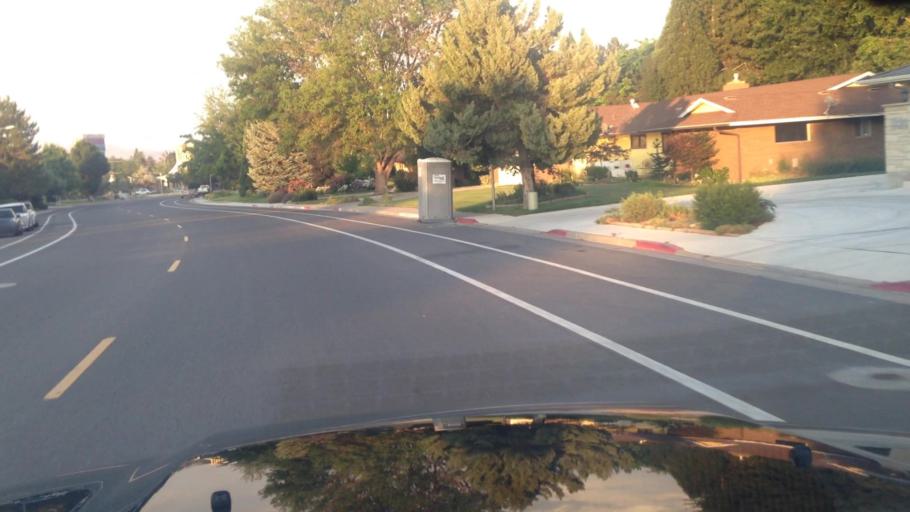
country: US
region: Nevada
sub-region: Washoe County
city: Reno
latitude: 39.4833
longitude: -119.8121
